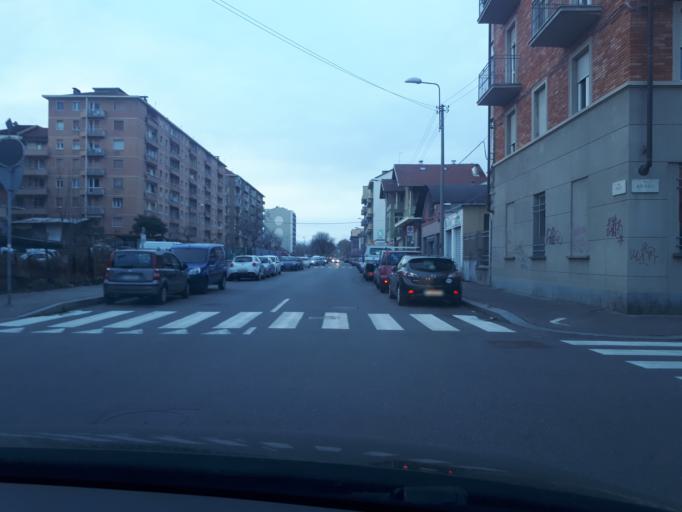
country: IT
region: Piedmont
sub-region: Provincia di Torino
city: Lesna
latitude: 45.0700
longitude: 7.6151
